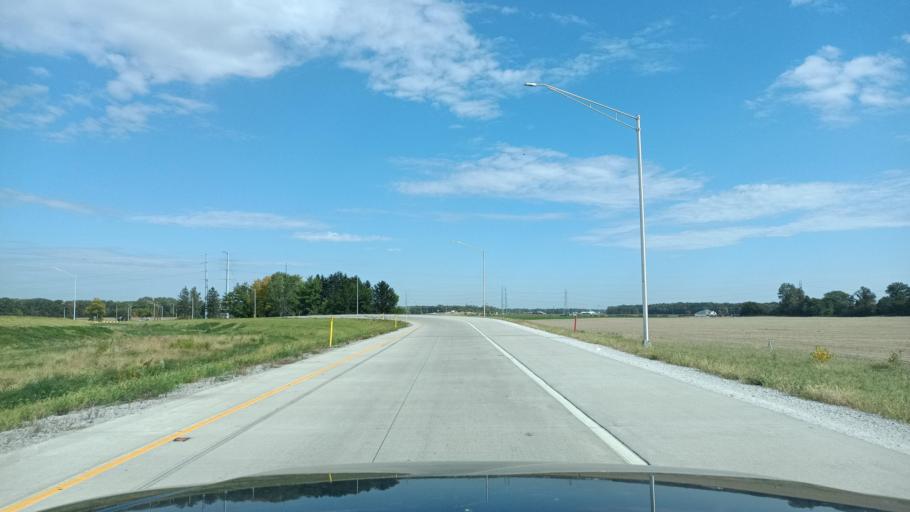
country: US
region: Indiana
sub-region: Allen County
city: New Haven
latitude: 41.0820
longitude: -84.9908
